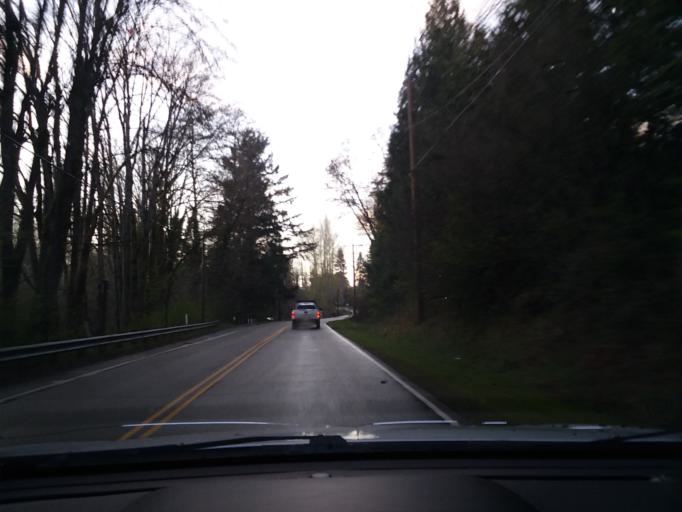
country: US
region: Washington
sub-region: King County
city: Kenmore
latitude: 47.7705
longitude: -122.2424
